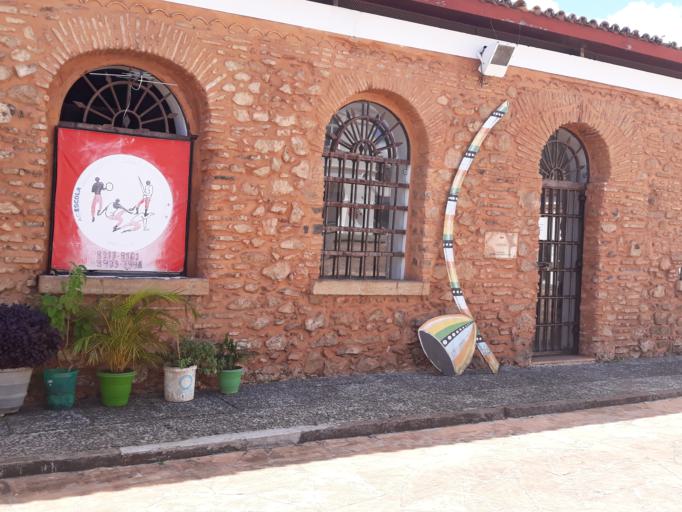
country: BR
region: Bahia
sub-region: Salvador
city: Salvador
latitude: -12.9625
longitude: -38.5033
